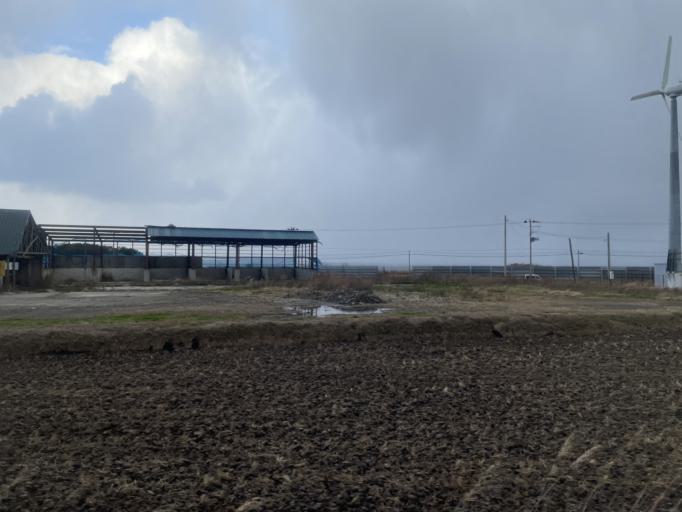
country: JP
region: Aomori
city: Mutsu
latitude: 41.1248
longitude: 141.2657
